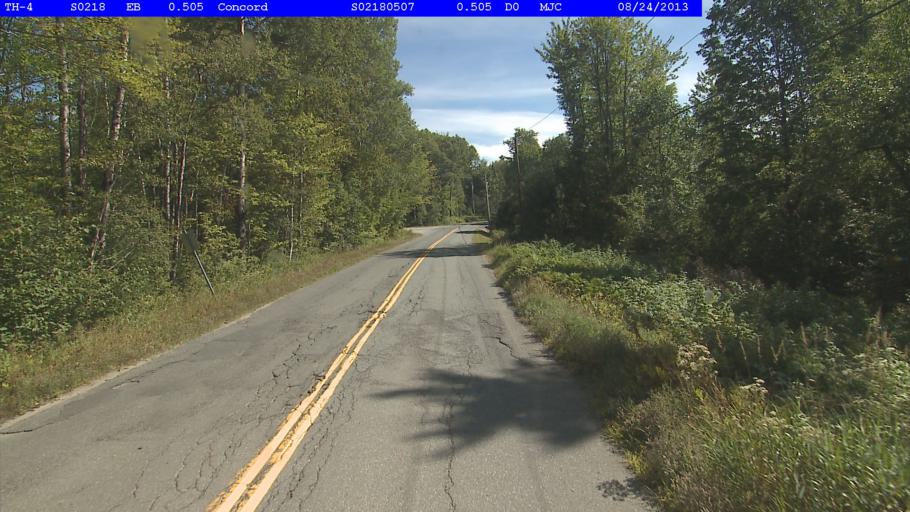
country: US
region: New Hampshire
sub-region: Grafton County
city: Littleton
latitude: 44.4582
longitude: -71.7712
